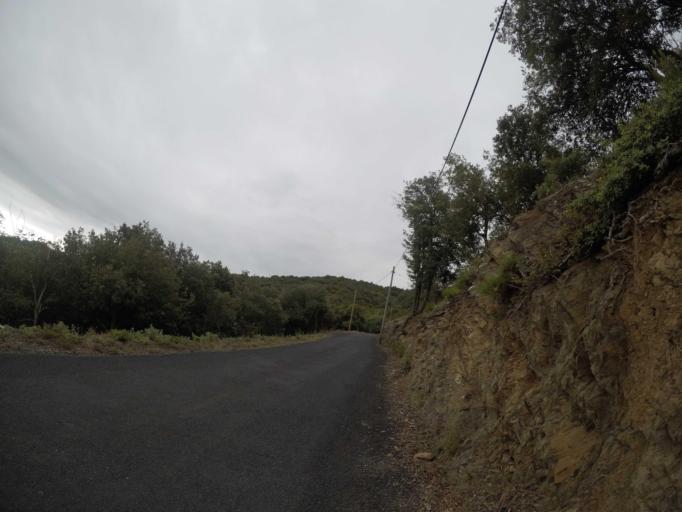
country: FR
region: Languedoc-Roussillon
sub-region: Departement des Pyrenees-Orientales
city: Ille-sur-Tet
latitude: 42.6233
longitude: 2.6190
